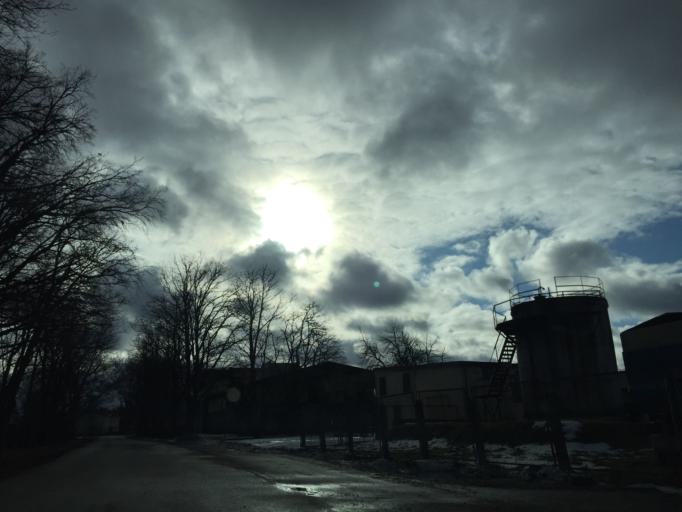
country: LV
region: Aloja
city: Aloja
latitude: 57.7731
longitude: 24.8130
